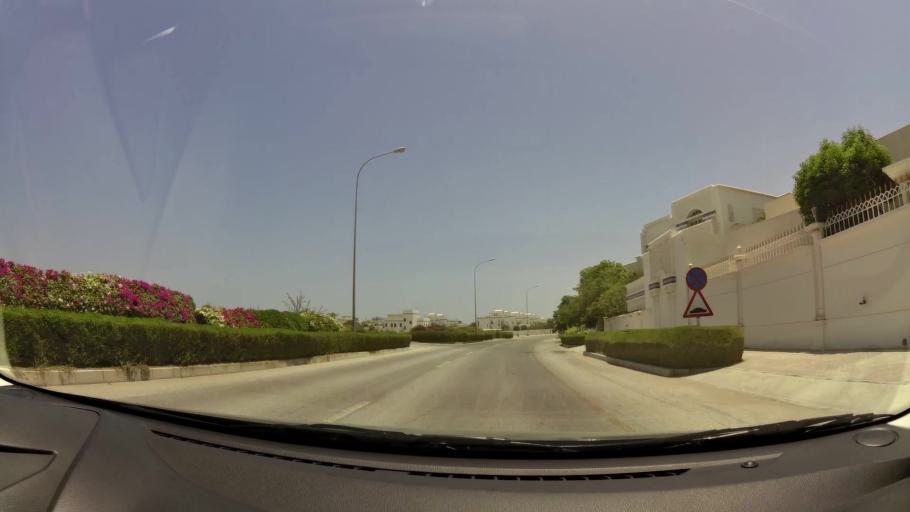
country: OM
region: Muhafazat Masqat
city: Bawshar
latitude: 23.6128
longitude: 58.4574
